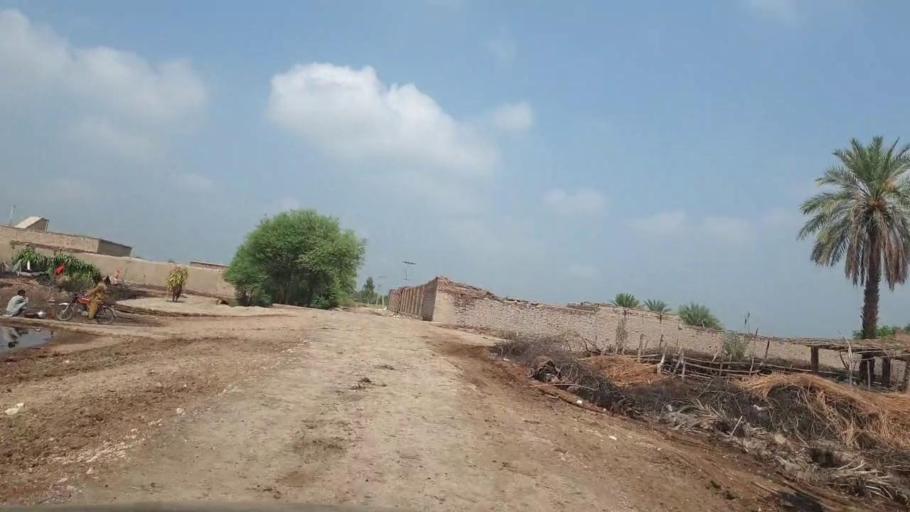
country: PK
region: Sindh
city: Pir jo Goth
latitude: 27.6048
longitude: 68.6986
